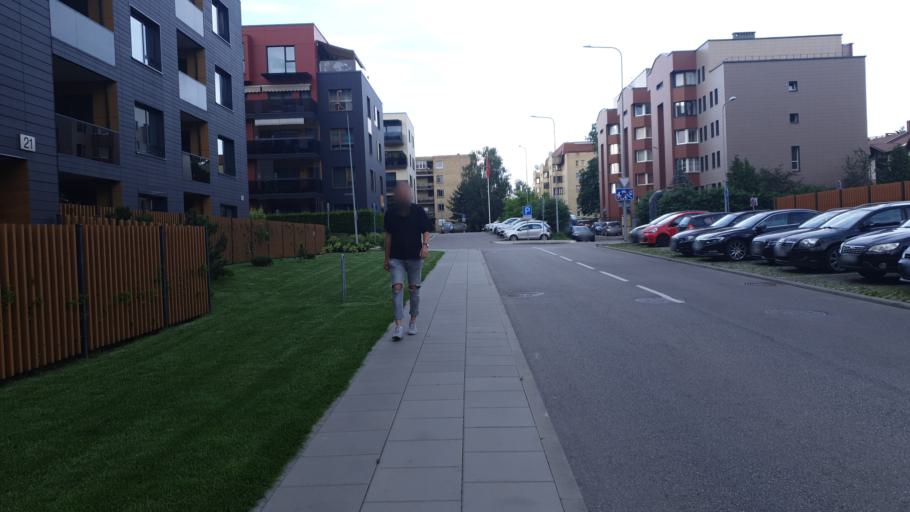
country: LT
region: Vilnius County
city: Rasos
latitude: 54.7253
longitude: 25.3217
